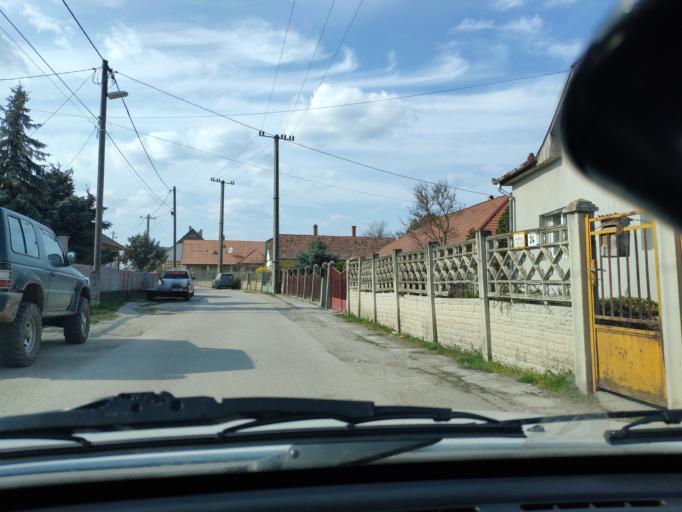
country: HU
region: Pest
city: Rackeve
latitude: 47.1640
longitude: 18.9415
